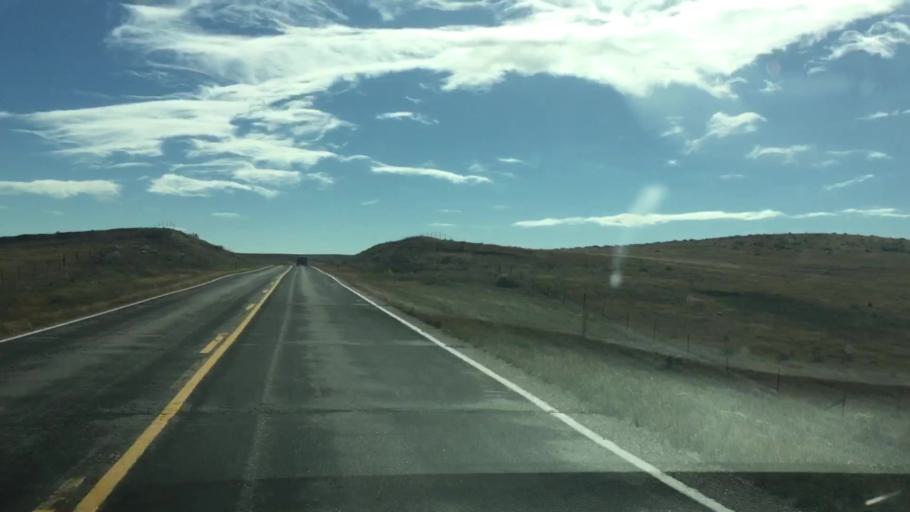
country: US
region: Colorado
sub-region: Elbert County
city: Kiowa
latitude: 39.2778
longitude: -104.2665
